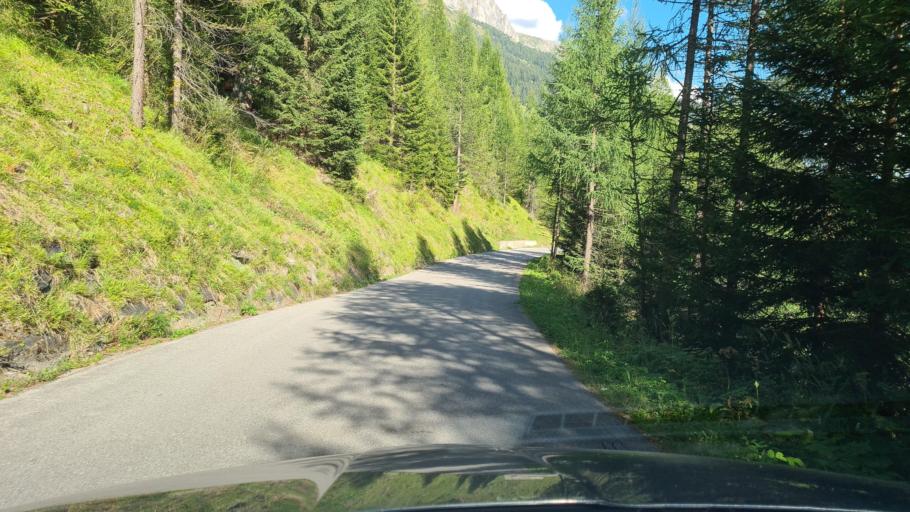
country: AT
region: Salzburg
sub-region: Politischer Bezirk Tamsweg
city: Zederhaus
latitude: 47.1857
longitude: 13.4261
